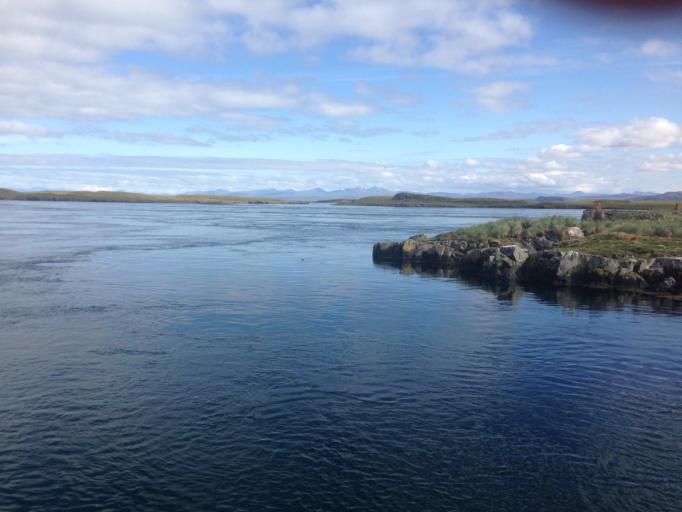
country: IS
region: West
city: Stykkisholmur
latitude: 65.1237
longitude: -22.4902
